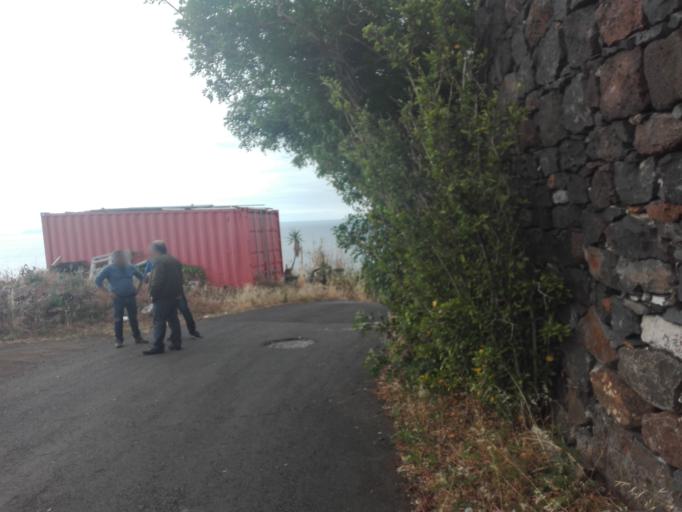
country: PT
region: Madeira
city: Canico
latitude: 32.6495
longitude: -16.8246
